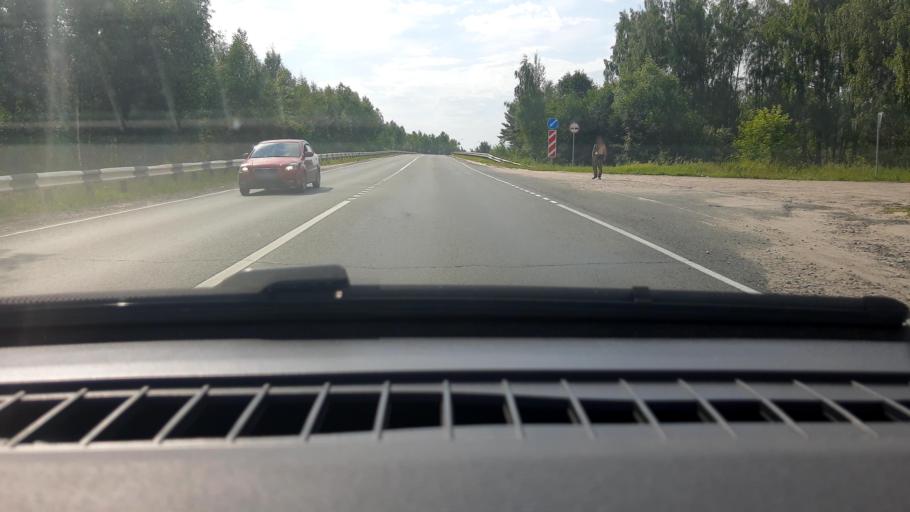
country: RU
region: Nizjnij Novgorod
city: Sitniki
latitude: 56.4732
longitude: 44.0328
